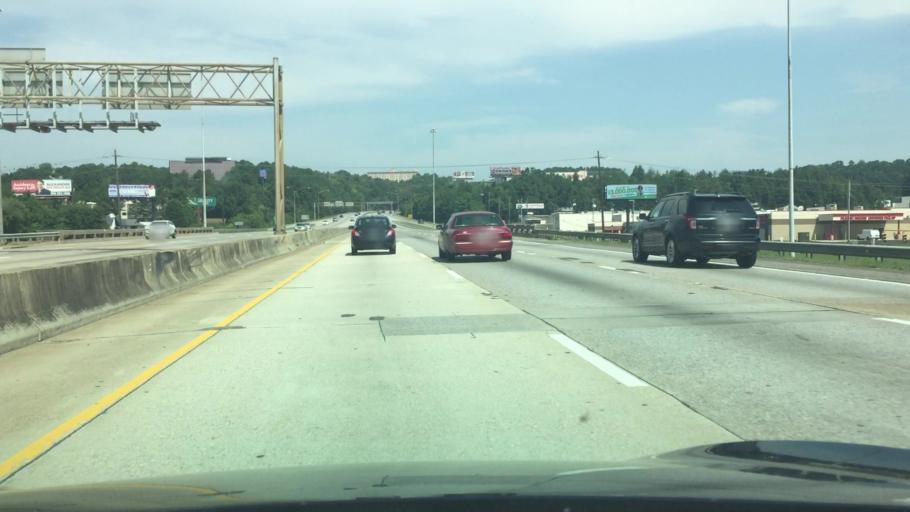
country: US
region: Alabama
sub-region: Jefferson County
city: Homewood
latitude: 33.4631
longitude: -86.8237
